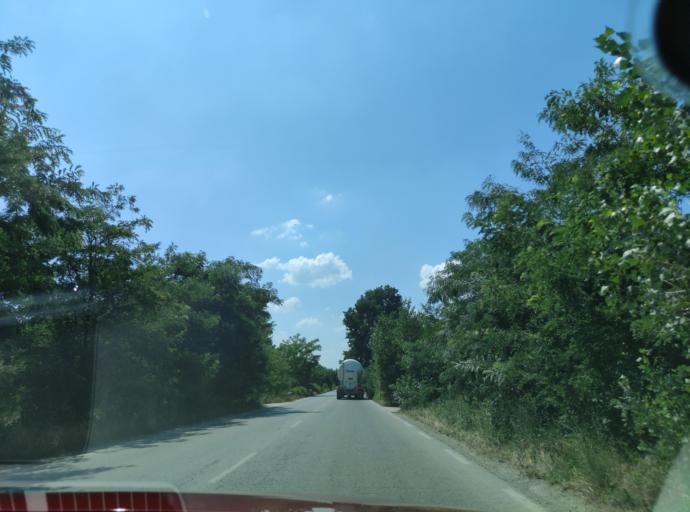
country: BG
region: Pleven
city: Iskur
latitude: 43.4540
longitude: 24.2396
